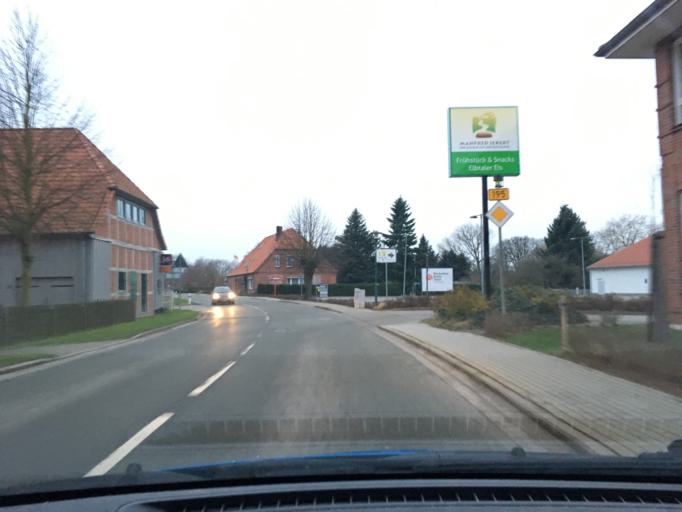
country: DE
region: Lower Saxony
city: Neu Darchau
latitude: 53.2861
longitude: 10.9282
